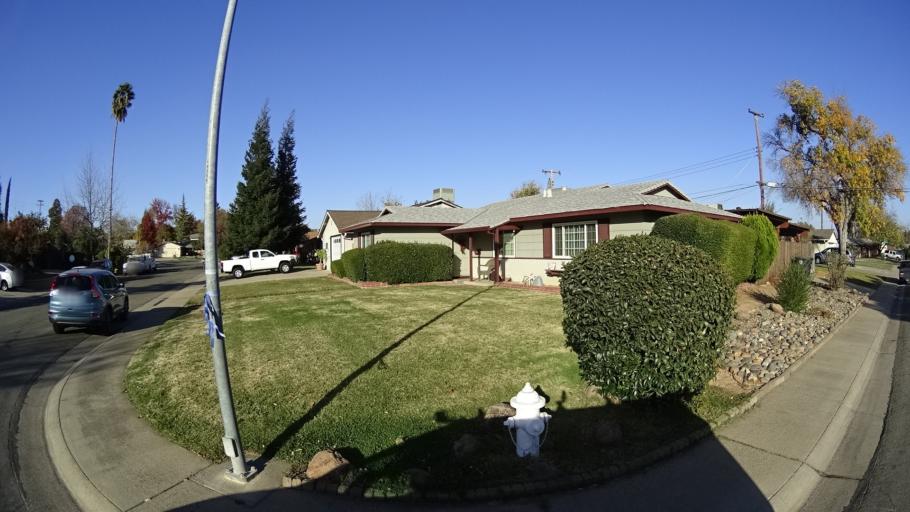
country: US
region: California
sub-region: Sacramento County
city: Antelope
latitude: 38.7023
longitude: -121.3075
